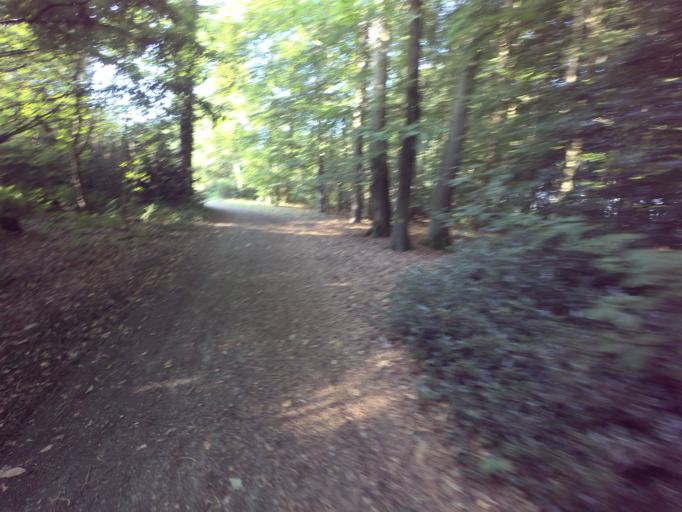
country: BE
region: Flanders
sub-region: Provincie Limburg
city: Sint-Pieters-Voeren
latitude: 50.7700
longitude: 5.8889
